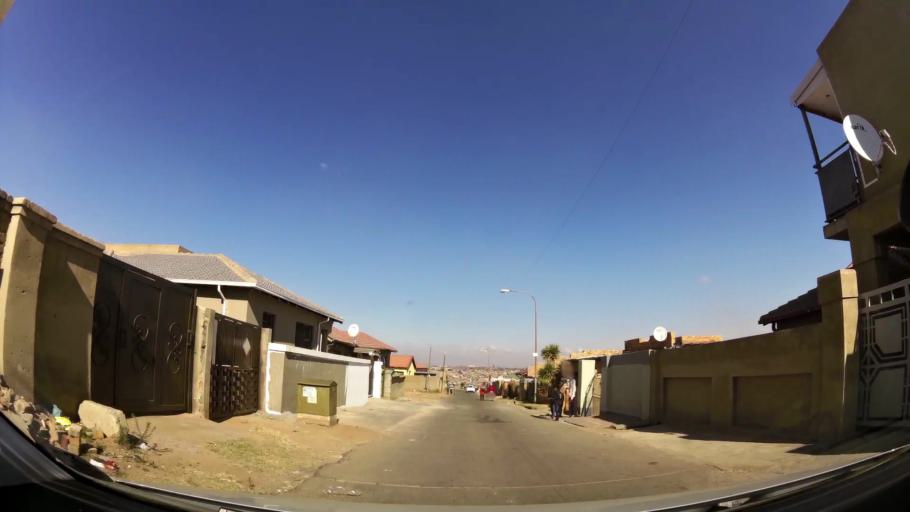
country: ZA
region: Gauteng
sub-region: City of Johannesburg Metropolitan Municipality
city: Roodepoort
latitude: -26.2173
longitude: 27.8873
